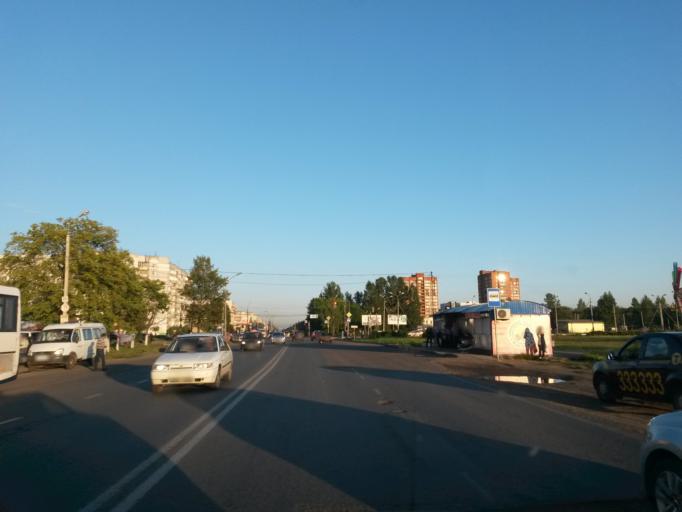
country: RU
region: Jaroslavl
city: Yaroslavl
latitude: 57.6987
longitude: 39.7628
